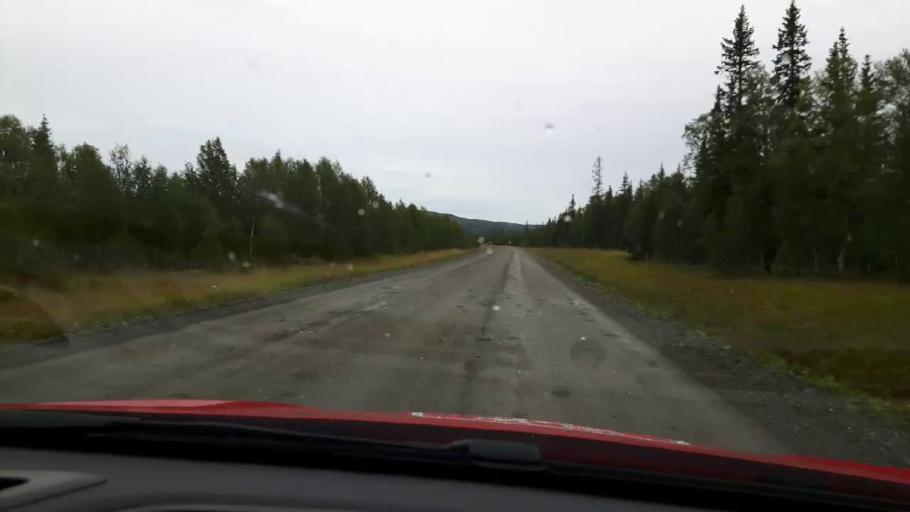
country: NO
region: Nord-Trondelag
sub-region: Meraker
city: Meraker
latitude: 63.5571
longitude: 12.3167
